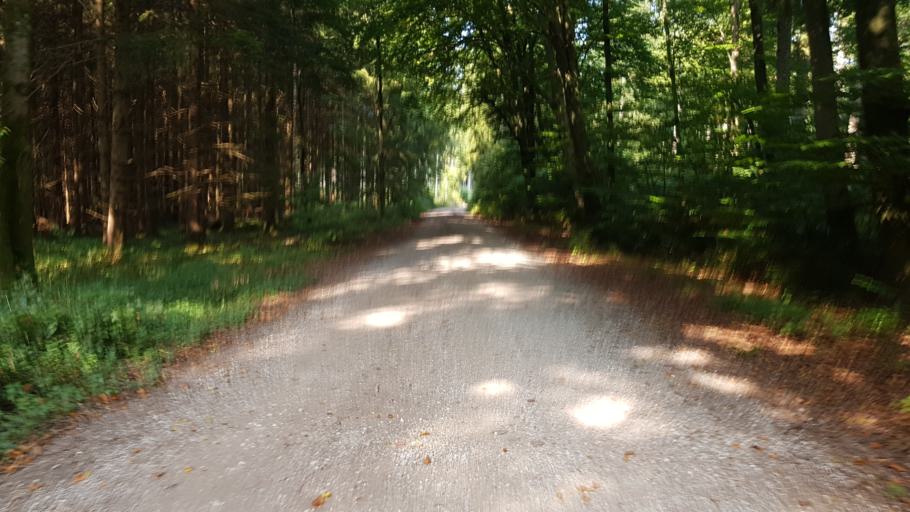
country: DE
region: Bavaria
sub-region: Upper Bavaria
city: Gilching
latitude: 48.0802
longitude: 11.3094
